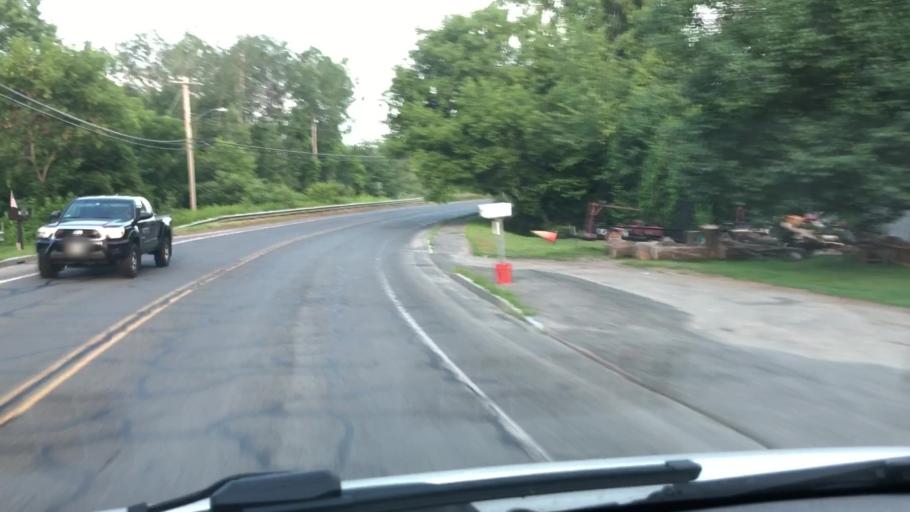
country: US
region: Massachusetts
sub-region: Berkshire County
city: Pittsfield
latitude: 42.4521
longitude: -73.2037
